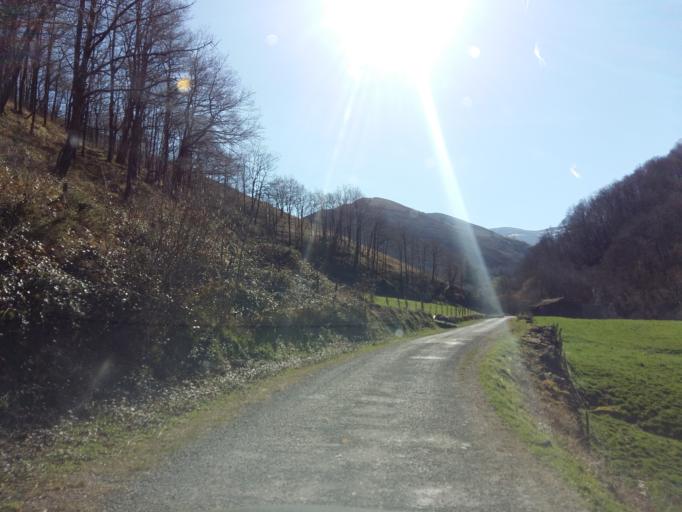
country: ES
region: Cantabria
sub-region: Provincia de Cantabria
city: Vega de Pas
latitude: 43.1343
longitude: -3.7875
